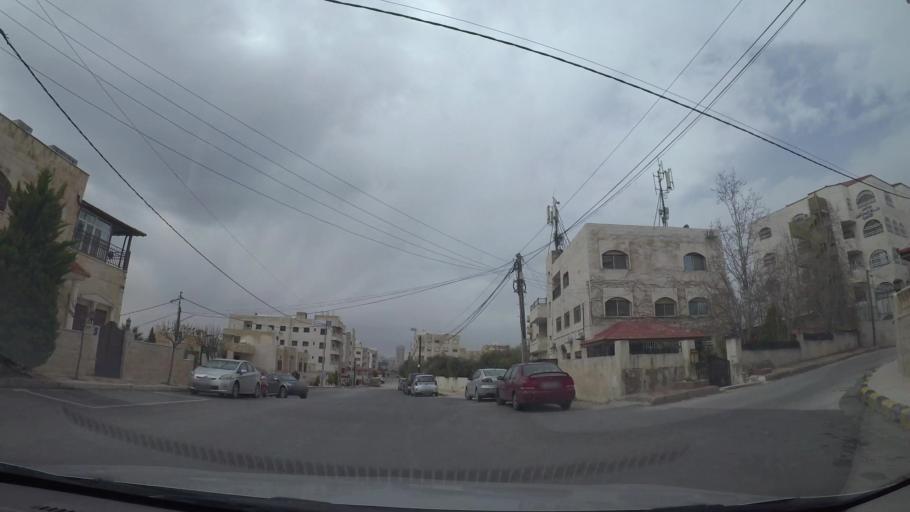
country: JO
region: Amman
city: Umm as Summaq
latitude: 31.9051
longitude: 35.8427
